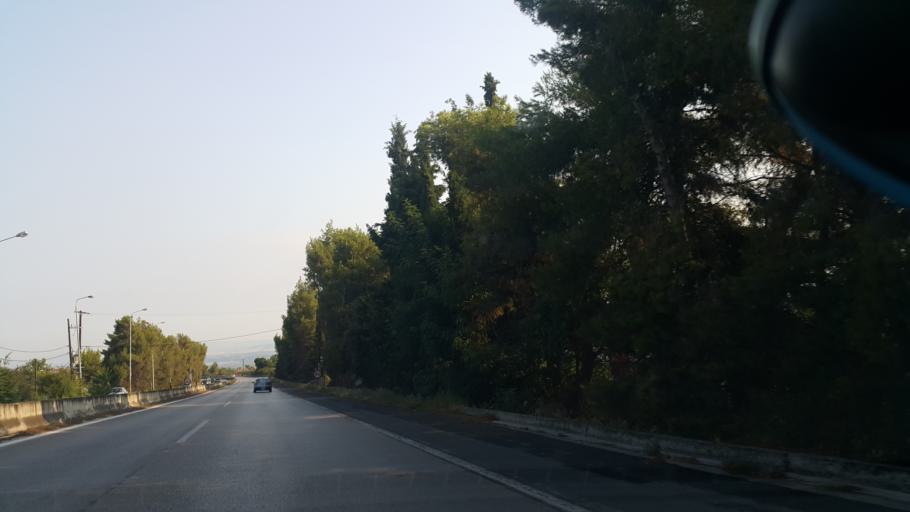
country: GR
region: Central Macedonia
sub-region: Nomos Thessalonikis
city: Kardia
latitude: 40.4628
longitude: 22.9982
